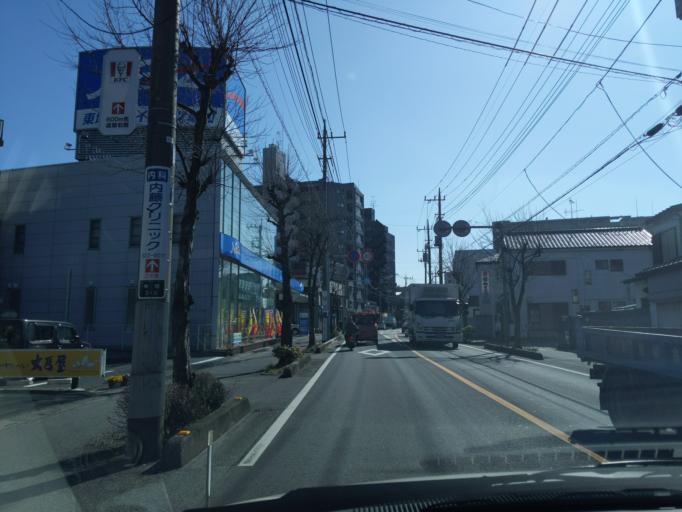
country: JP
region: Saitama
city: Soka
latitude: 35.8354
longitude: 139.8072
